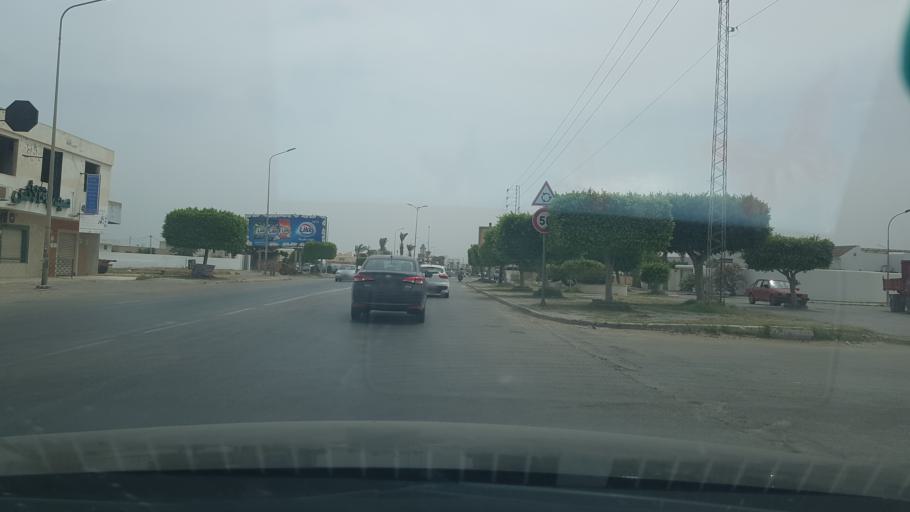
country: TN
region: Safaqis
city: Al Qarmadah
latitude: 34.8262
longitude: 10.7637
